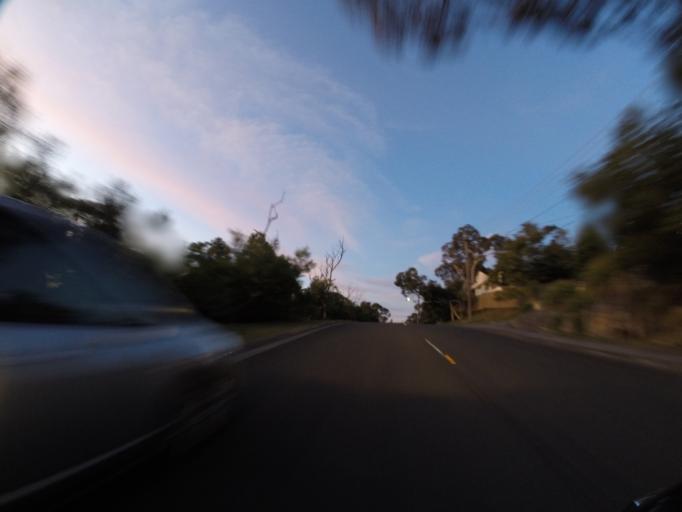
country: AU
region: New South Wales
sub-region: Sutherland Shire
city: Heathcote
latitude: -34.0916
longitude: 151.0004
